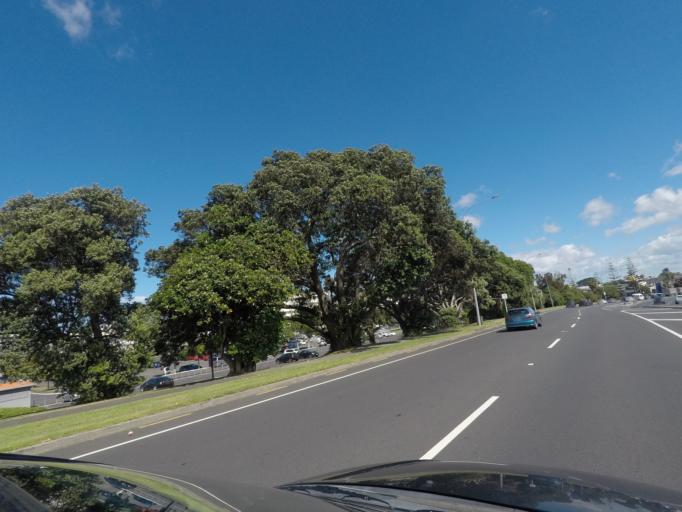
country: NZ
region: Auckland
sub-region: Auckland
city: Manukau City
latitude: -36.9914
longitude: 174.8844
